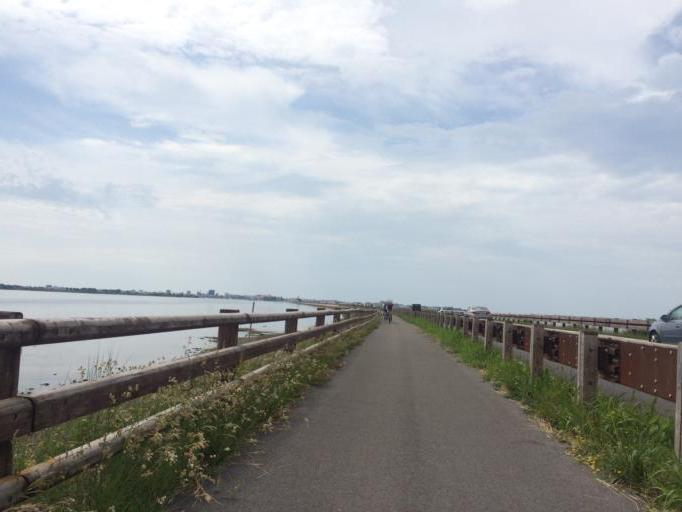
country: IT
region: Friuli Venezia Giulia
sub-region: Provincia di Gorizia
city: Grado
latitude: 45.7078
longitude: 13.3829
